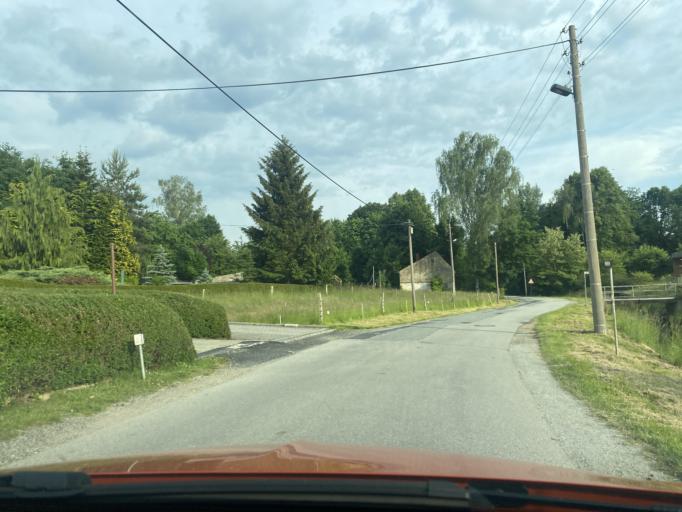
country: DE
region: Saxony
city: Herrnhut
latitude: 51.0235
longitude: 14.7794
